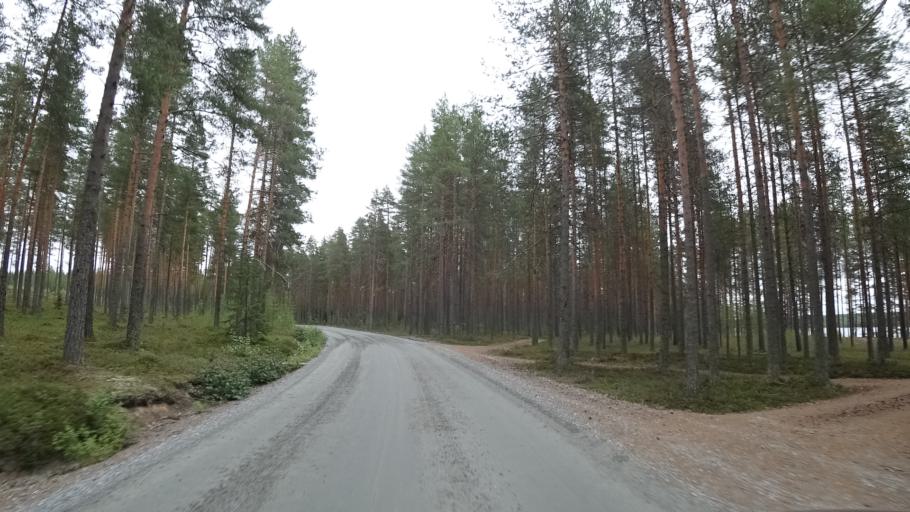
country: FI
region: North Karelia
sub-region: Pielisen Karjala
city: Lieksa
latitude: 63.3782
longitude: 30.3464
